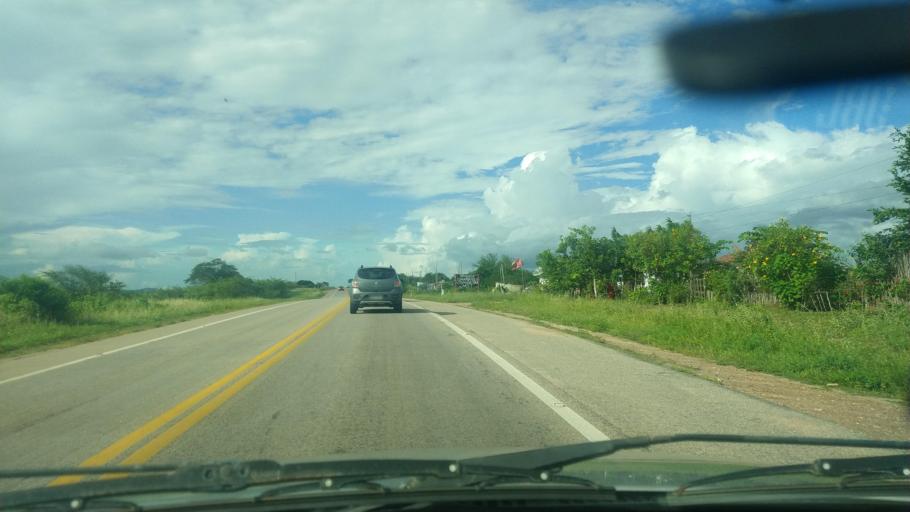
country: BR
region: Rio Grande do Norte
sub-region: Tangara
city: Tangara
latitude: -6.1814
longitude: -35.7723
